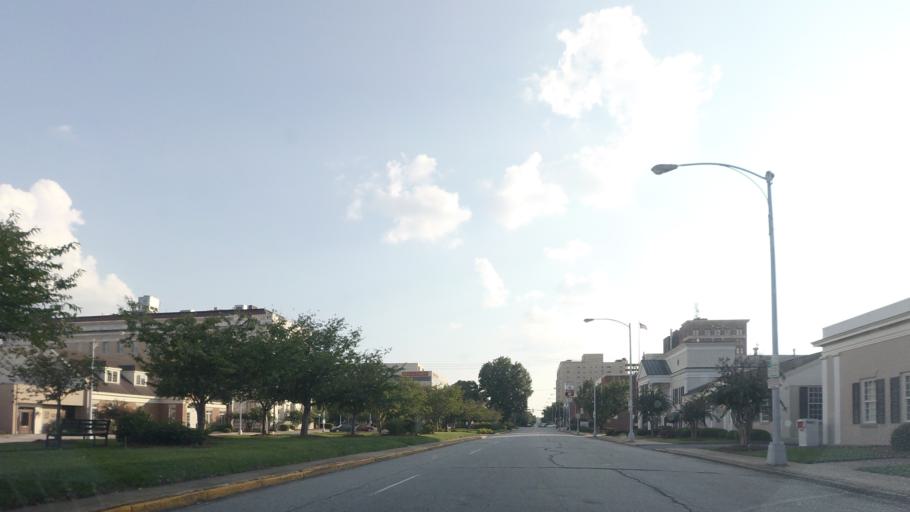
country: US
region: Georgia
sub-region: Bibb County
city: Macon
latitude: 32.8383
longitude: -83.6255
